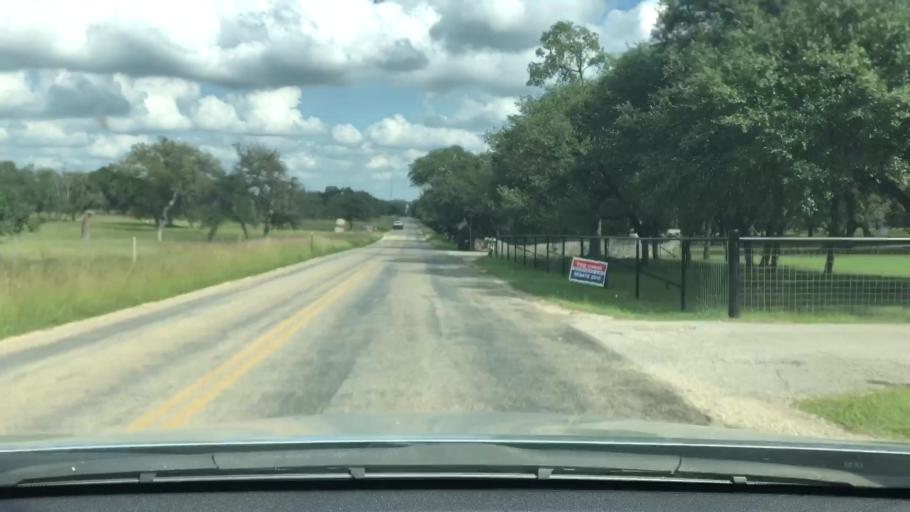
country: US
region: Texas
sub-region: Bexar County
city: Fair Oaks Ranch
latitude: 29.7858
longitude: -98.6590
